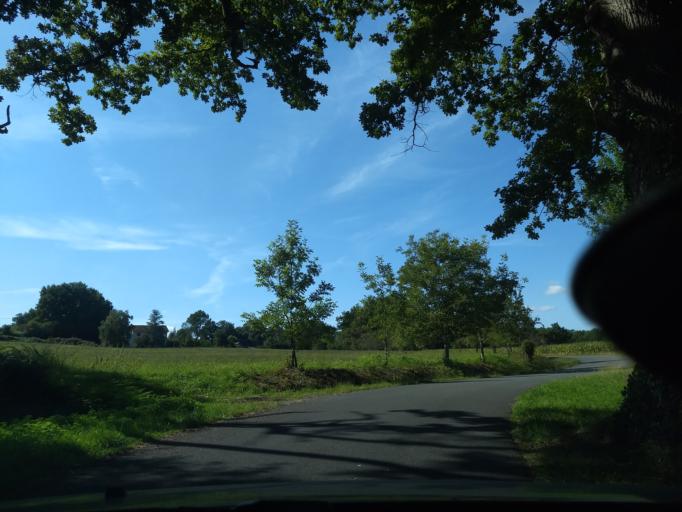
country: FR
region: Aquitaine
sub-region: Departement des Pyrenees-Atlantiques
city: Soumoulou
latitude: 43.2950
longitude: -0.1557
